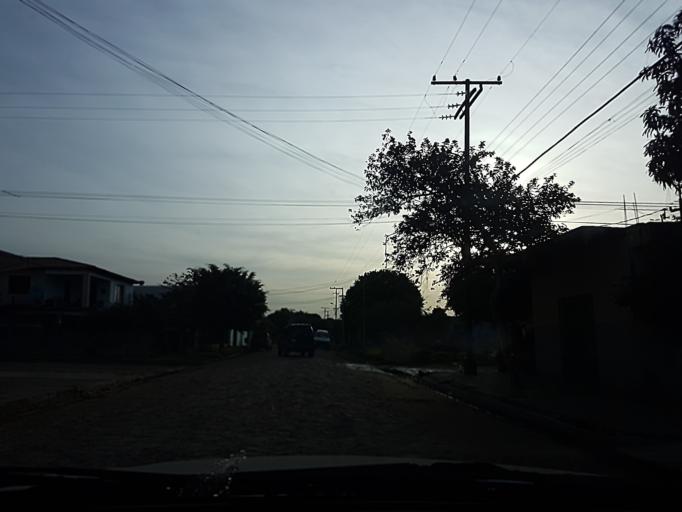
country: PY
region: Central
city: Colonia Mariano Roque Alonso
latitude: -25.2089
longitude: -57.5375
